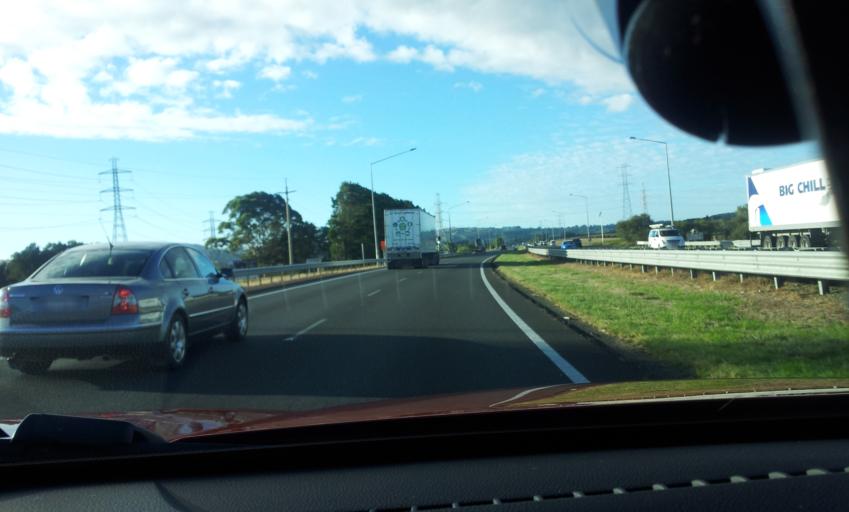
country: NZ
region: Auckland
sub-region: Auckland
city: Papakura
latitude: -37.1204
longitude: 174.9557
